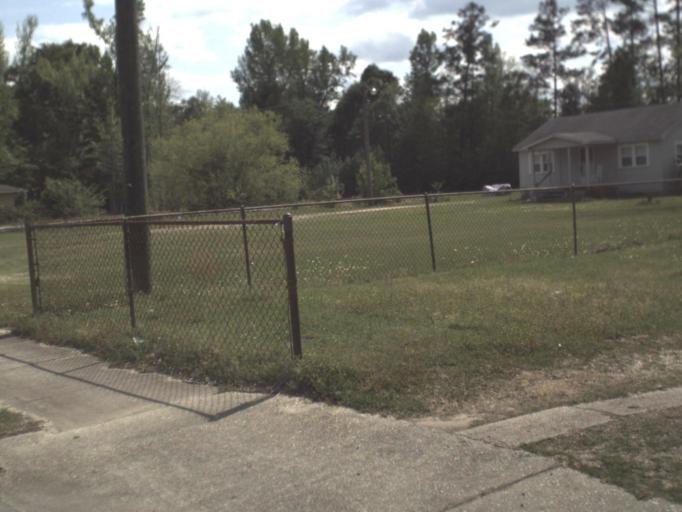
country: US
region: Alabama
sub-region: Escambia County
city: Flomaton
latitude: 30.9919
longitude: -87.2576
